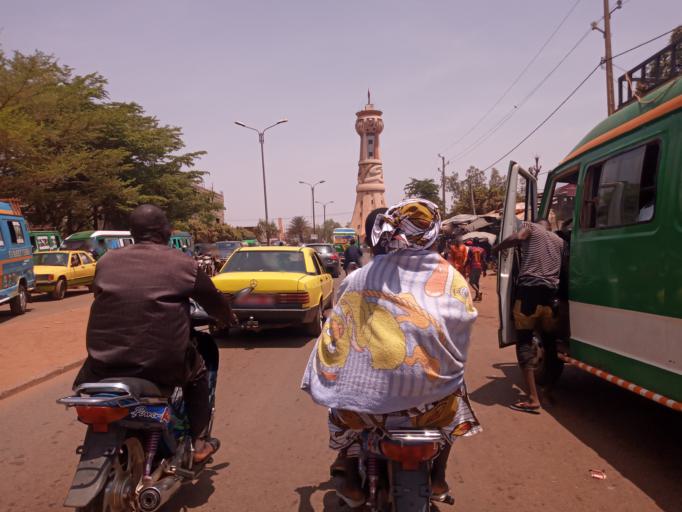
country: ML
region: Bamako
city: Bamako
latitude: 12.5835
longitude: -7.9442
